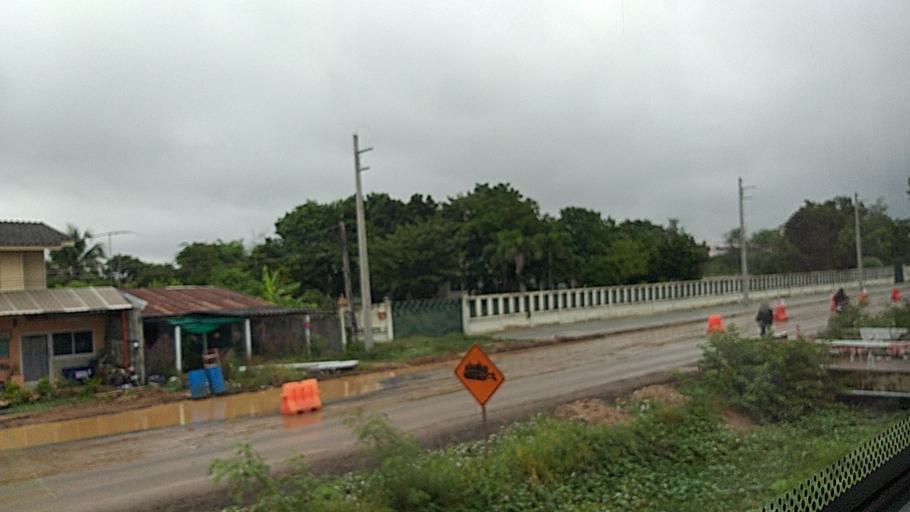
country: TH
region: Nakhon Ratchasima
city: Nakhon Ratchasima
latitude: 14.9951
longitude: 102.0698
